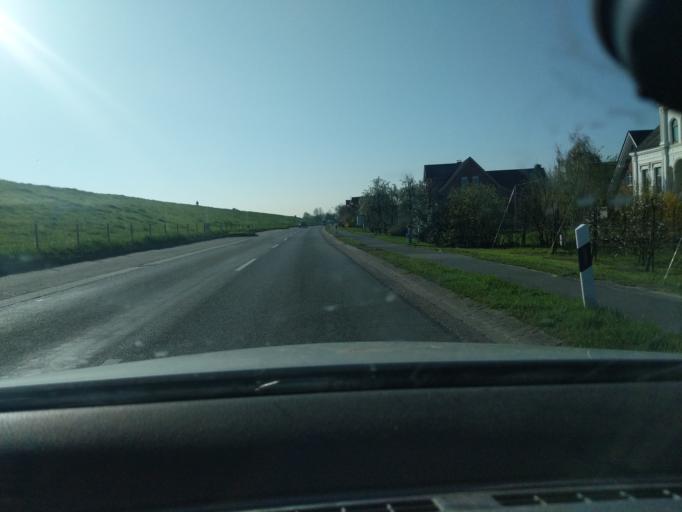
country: DE
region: Lower Saxony
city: Mittelnkirchen
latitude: 53.5654
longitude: 9.6499
